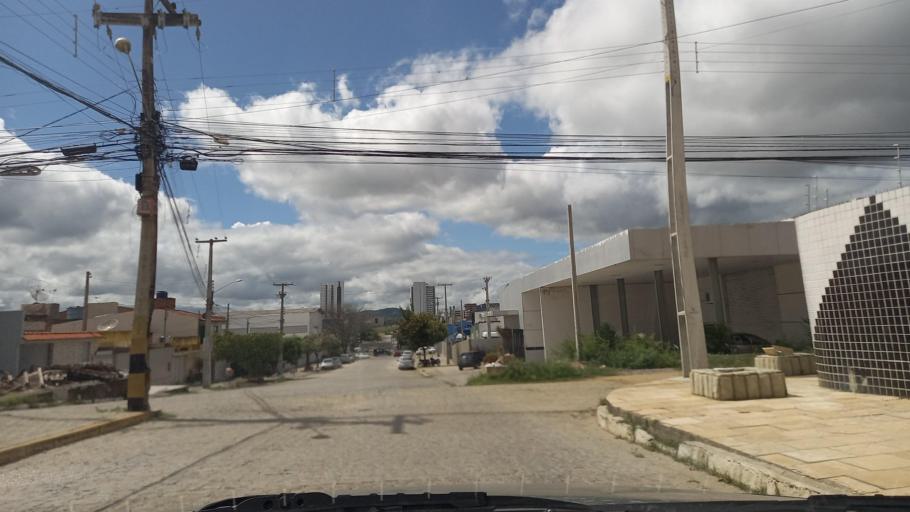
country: BR
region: Pernambuco
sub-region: Caruaru
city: Caruaru
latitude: -8.2579
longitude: -35.9776
